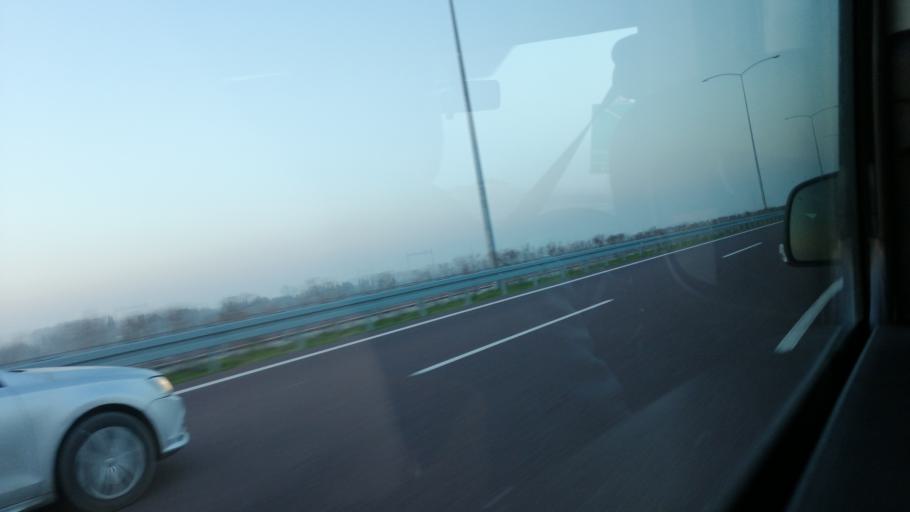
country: TR
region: Yalova
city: Altinova
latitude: 40.7096
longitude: 29.4958
